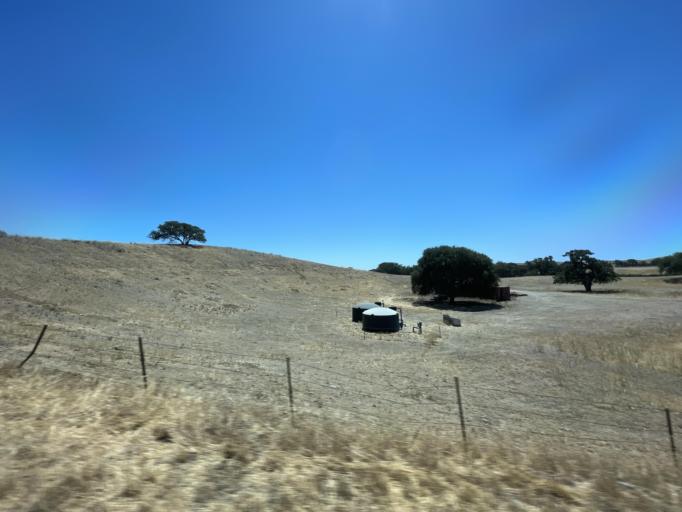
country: US
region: California
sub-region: San Luis Obispo County
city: Paso Robles
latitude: 35.6409
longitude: -120.5796
